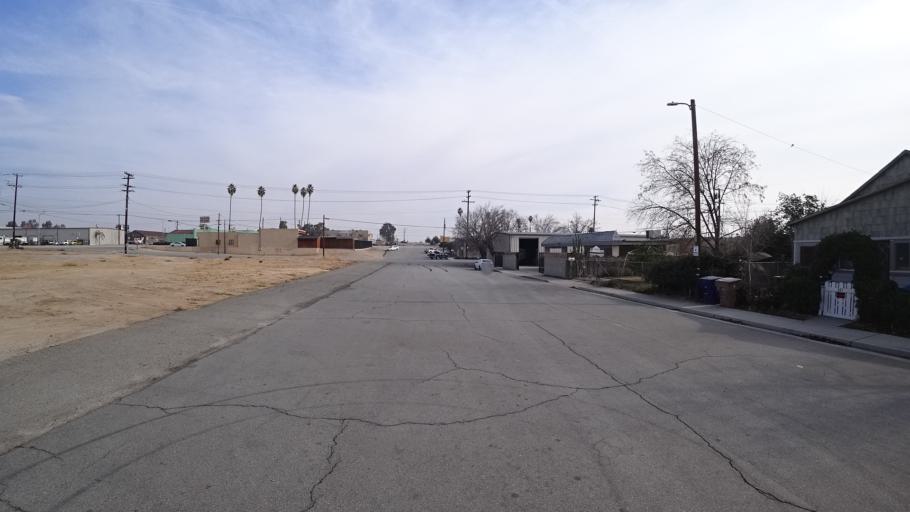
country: US
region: California
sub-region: Kern County
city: Bakersfield
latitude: 35.3790
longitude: -119.0056
